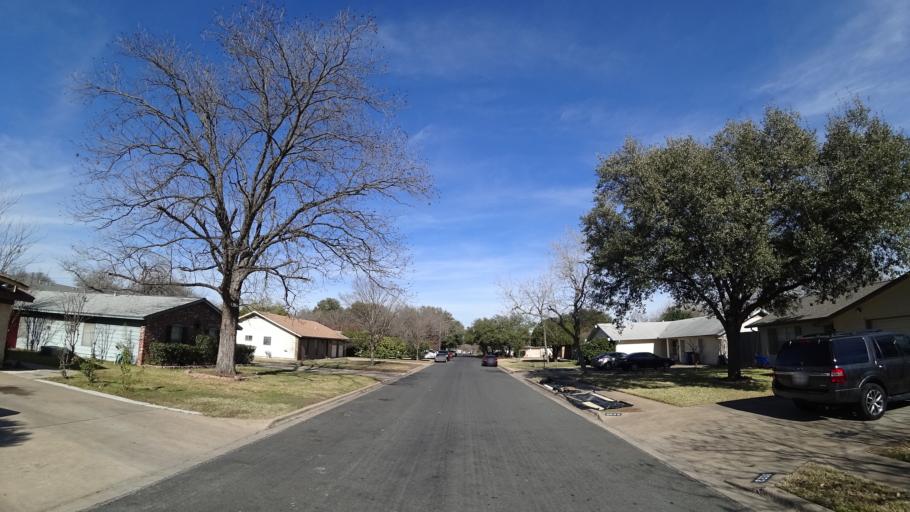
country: US
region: Texas
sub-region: Travis County
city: Wells Branch
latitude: 30.3731
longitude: -97.7104
